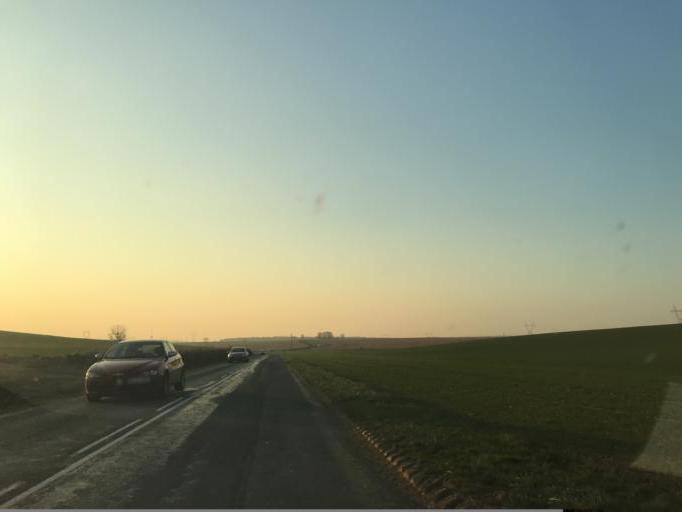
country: FR
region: Ile-de-France
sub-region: Departement de Seine-et-Marne
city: Charny
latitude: 49.0117
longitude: 2.7503
